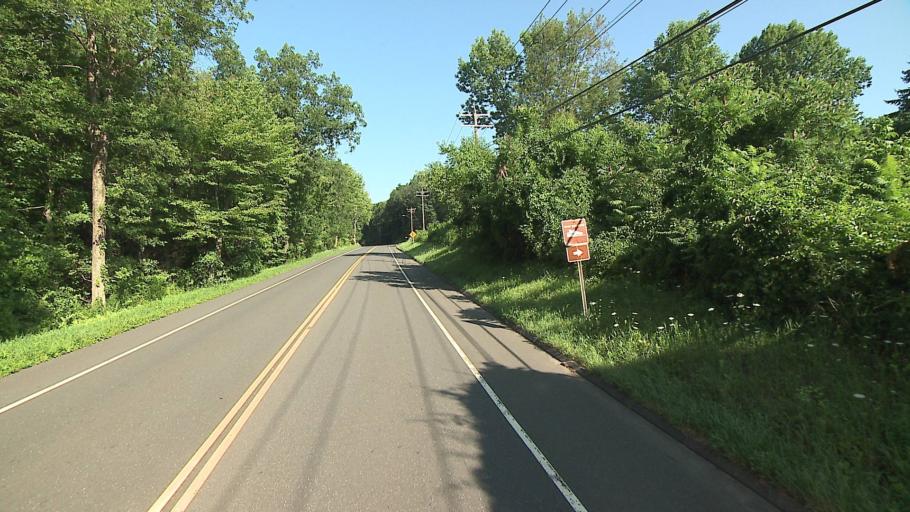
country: US
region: Connecticut
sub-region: Litchfield County
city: Litchfield
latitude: 41.8433
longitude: -73.2810
